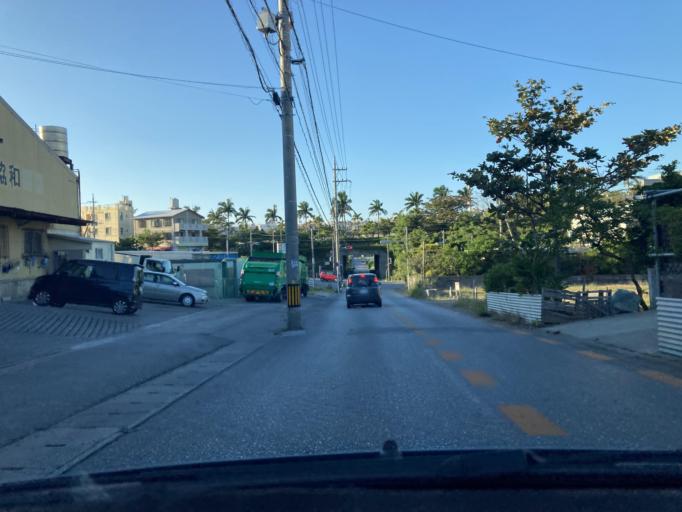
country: JP
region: Okinawa
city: Naha-shi
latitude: 26.2115
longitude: 127.7299
